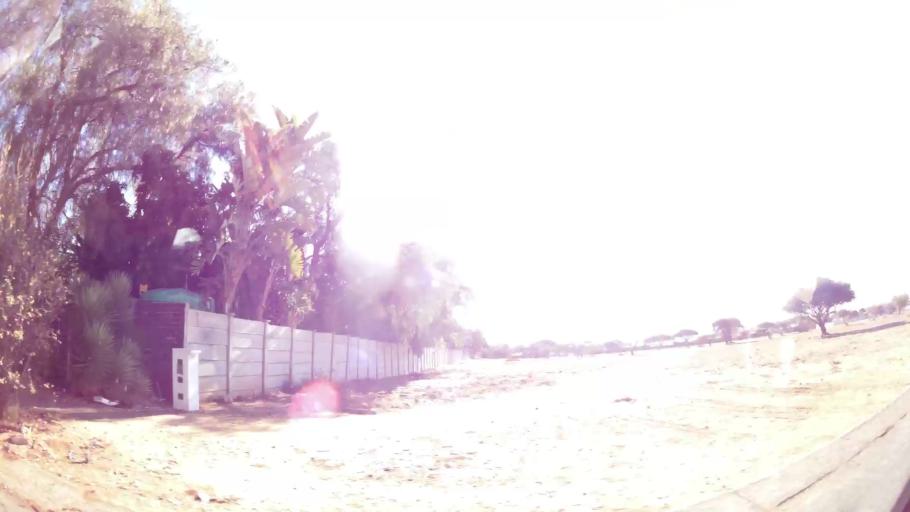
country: ZA
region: Limpopo
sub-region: Capricorn District Municipality
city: Polokwane
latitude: -23.8851
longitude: 29.4874
